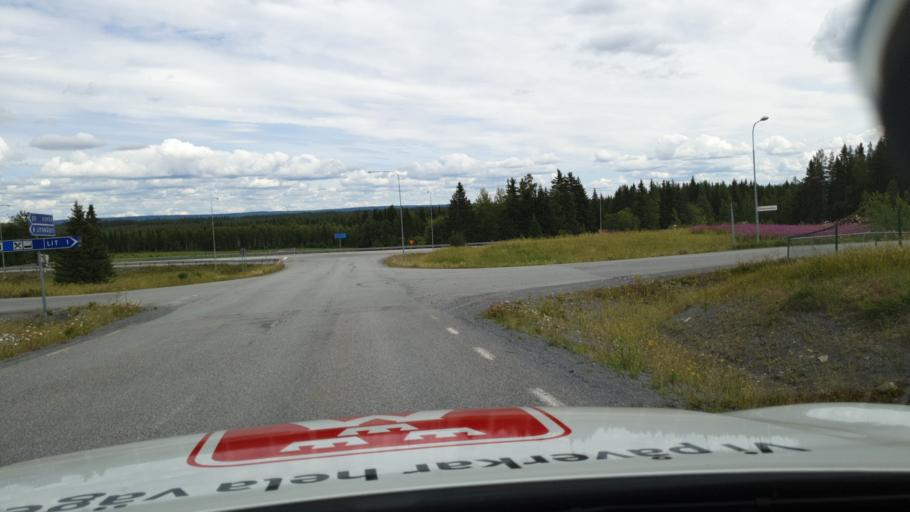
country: SE
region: Jaemtland
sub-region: OEstersunds Kommun
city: Lit
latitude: 63.3301
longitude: 14.8549
